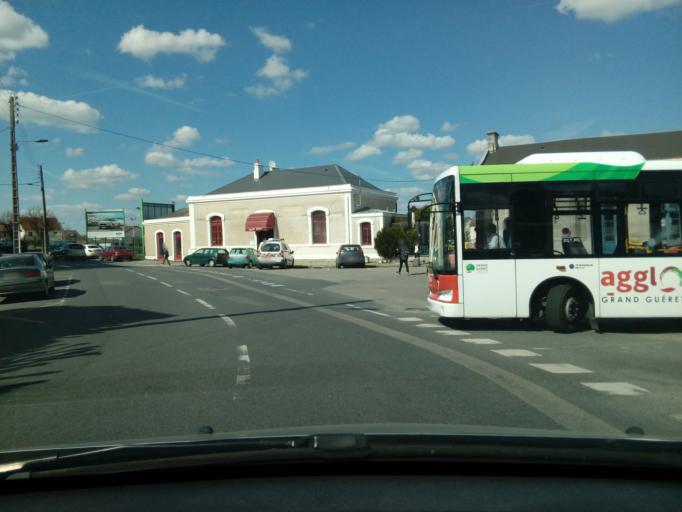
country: FR
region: Limousin
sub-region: Departement de la Creuse
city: Gueret
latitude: 46.1739
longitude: 1.8788
